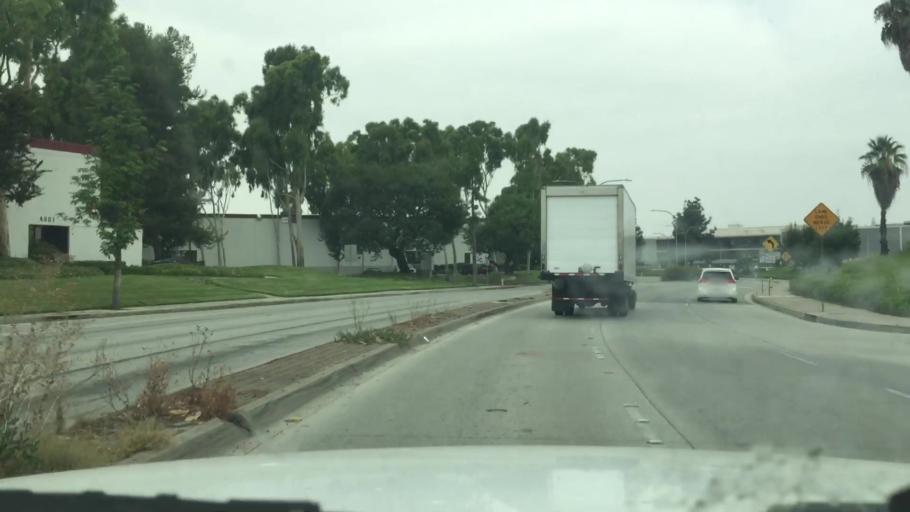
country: US
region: California
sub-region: Los Angeles County
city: Commerce
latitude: 33.9923
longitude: -118.1614
